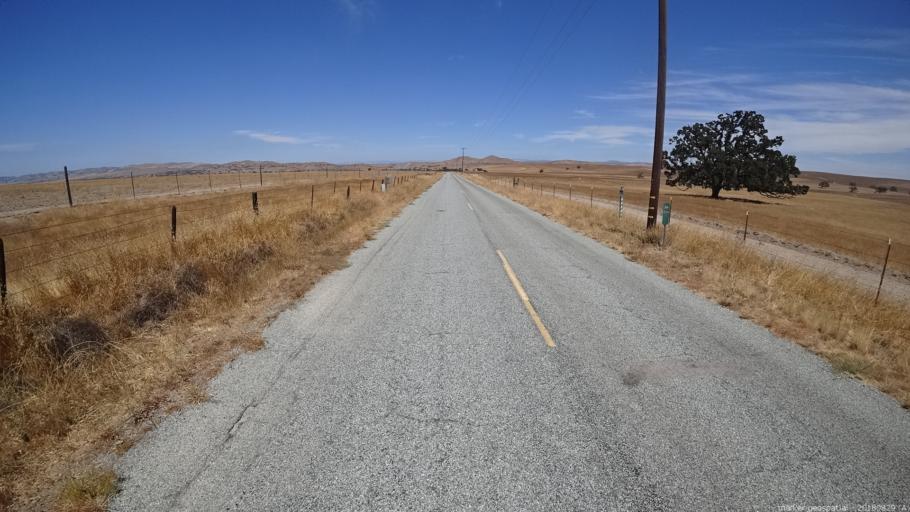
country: US
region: California
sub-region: San Luis Obispo County
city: Lake Nacimiento
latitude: 35.8394
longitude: -120.8430
